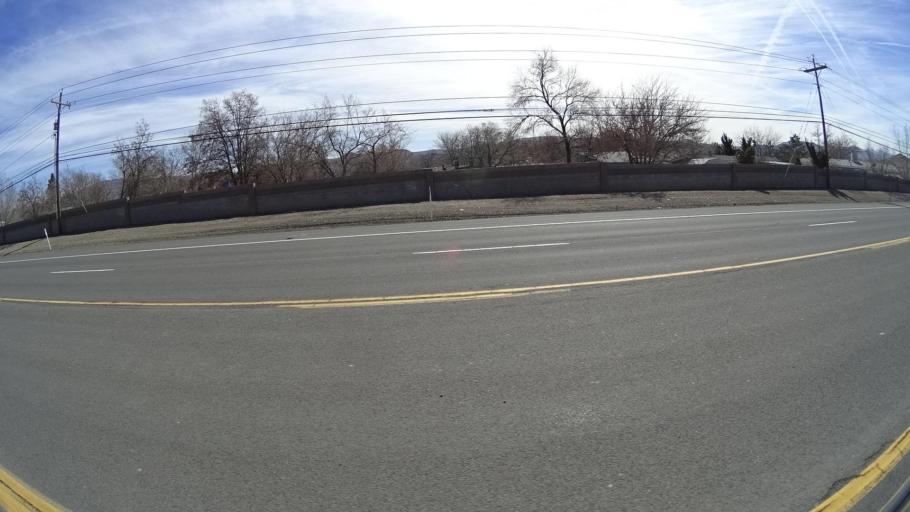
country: US
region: Nevada
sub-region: Washoe County
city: Sun Valley
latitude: 39.5901
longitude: -119.7404
